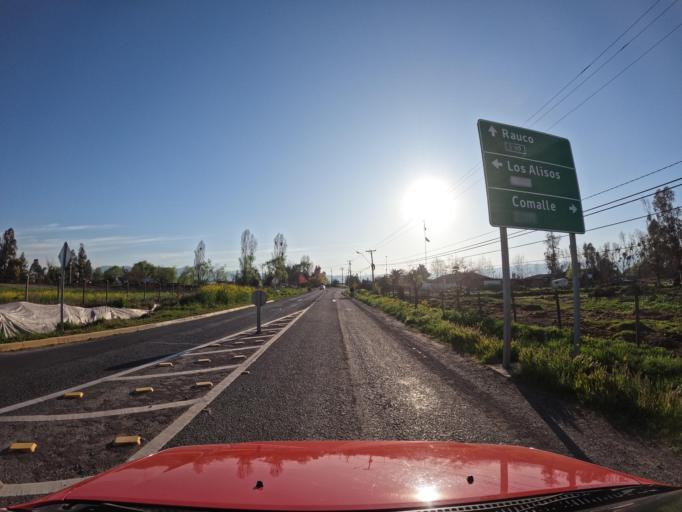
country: CL
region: Maule
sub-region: Provincia de Curico
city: Rauco
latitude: -34.8683
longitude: -71.2627
